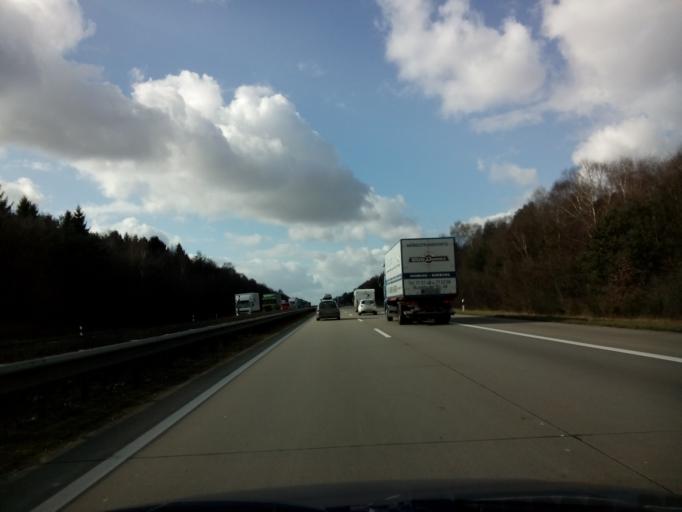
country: DE
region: Lower Saxony
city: Prinzhofte
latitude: 52.9537
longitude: 8.5554
